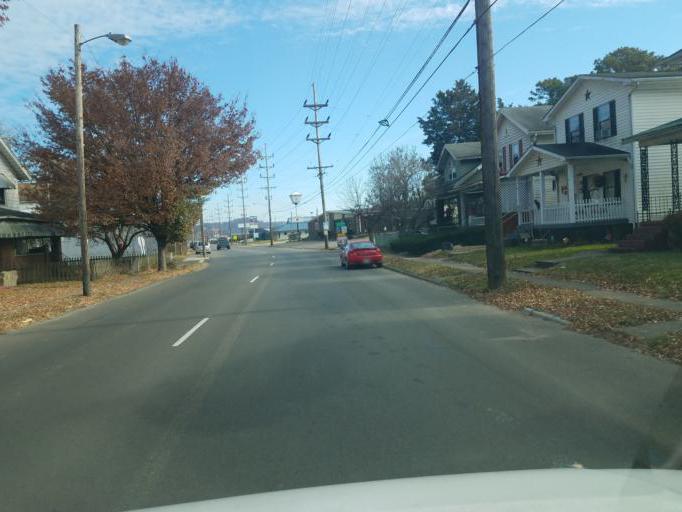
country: US
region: Ohio
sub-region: Scioto County
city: New Boston
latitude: 38.7438
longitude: -82.9512
